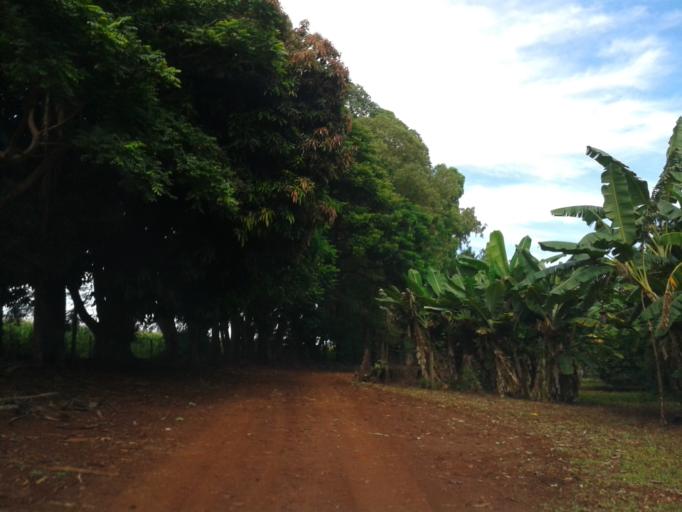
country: BR
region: Minas Gerais
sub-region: Capinopolis
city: Capinopolis
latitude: -18.6237
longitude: -49.7451
